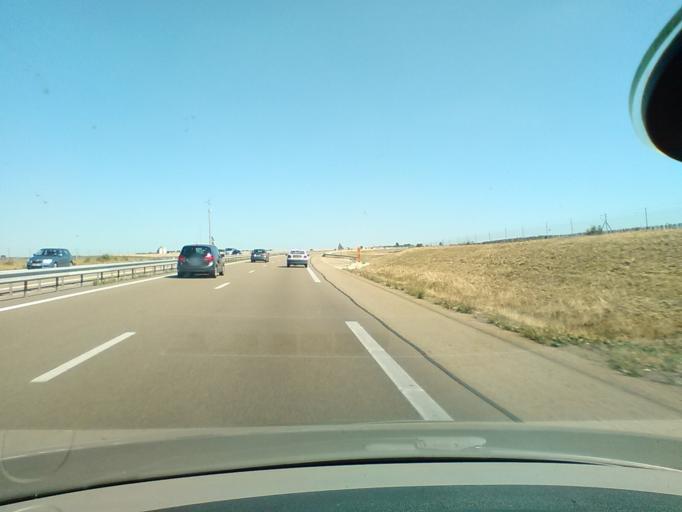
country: FR
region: Bourgogne
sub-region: Departement de l'Yonne
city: Saint-Bris-le-Vineux
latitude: 47.7728
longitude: 3.7185
